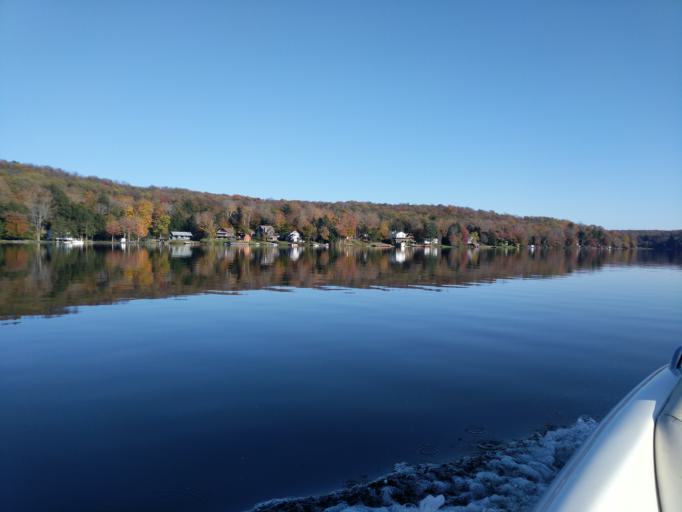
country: US
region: New York
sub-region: Sullivan County
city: Livingston Manor
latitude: 41.8909
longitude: -74.9807
